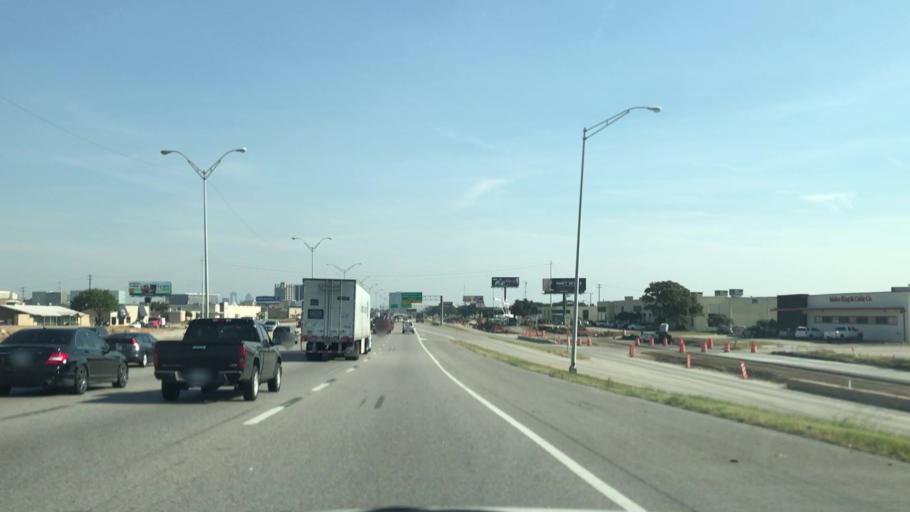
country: US
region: Texas
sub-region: Dallas County
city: Irving
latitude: 32.8266
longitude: -96.8848
